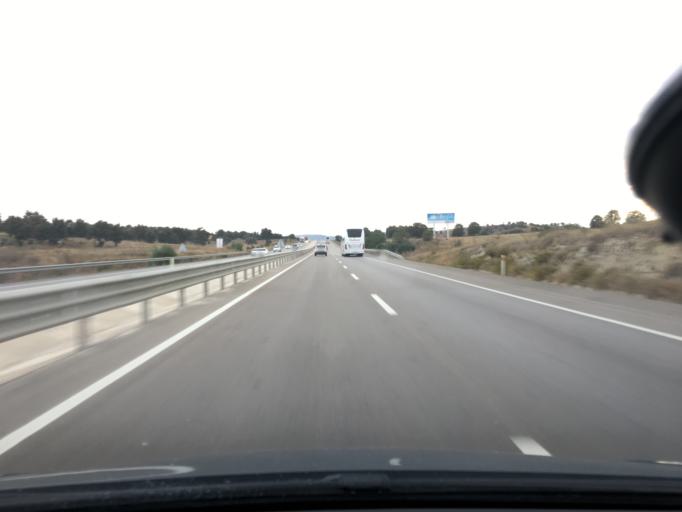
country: TR
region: Afyonkarahisar
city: Sincanli
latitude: 38.6521
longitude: 30.3173
